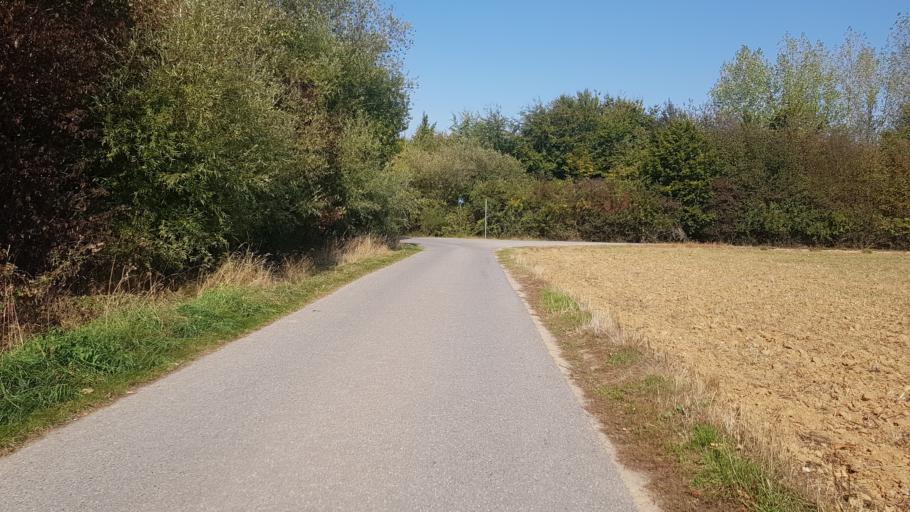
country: DE
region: North Rhine-Westphalia
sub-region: Regierungsbezirk Koln
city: Eschweiler
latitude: 50.8492
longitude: 6.2630
